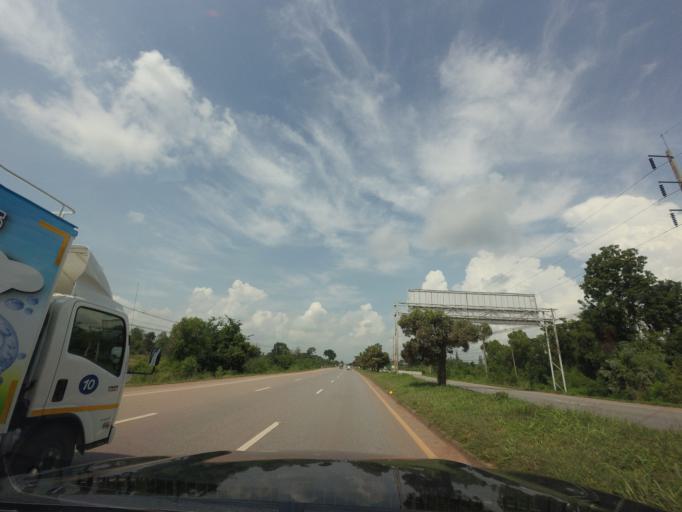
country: TH
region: Khon Kaen
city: Ban Fang
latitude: 16.4505
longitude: 102.7350
